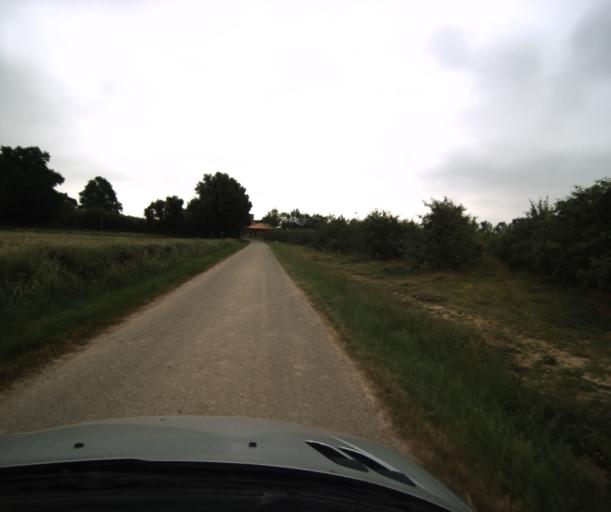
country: FR
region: Midi-Pyrenees
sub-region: Departement du Tarn-et-Garonne
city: Saint-Nicolas-de-la-Grave
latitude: 44.0649
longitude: 0.9853
